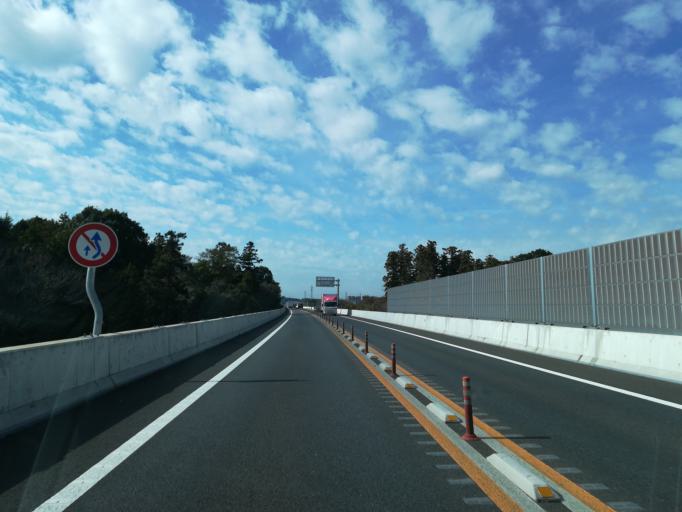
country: JP
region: Ibaraki
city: Naka
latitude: 36.0579
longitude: 140.0812
